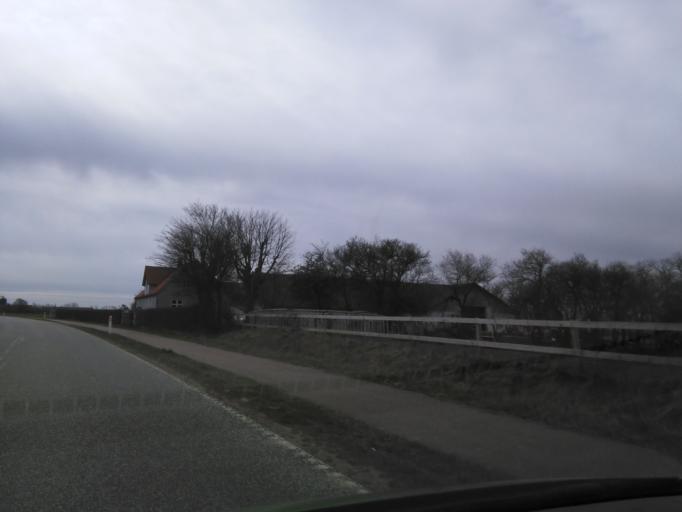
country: DK
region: Central Jutland
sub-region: Arhus Kommune
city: Malling
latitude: 56.0091
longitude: 10.2573
